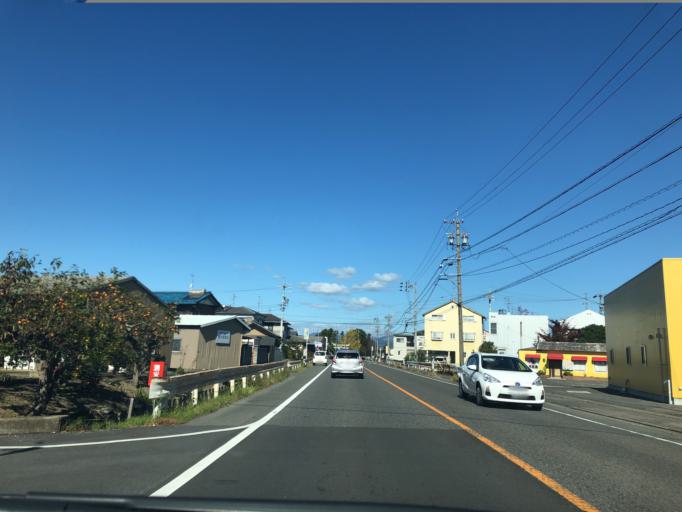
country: JP
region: Gifu
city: Ogaki
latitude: 35.3800
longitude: 136.6684
